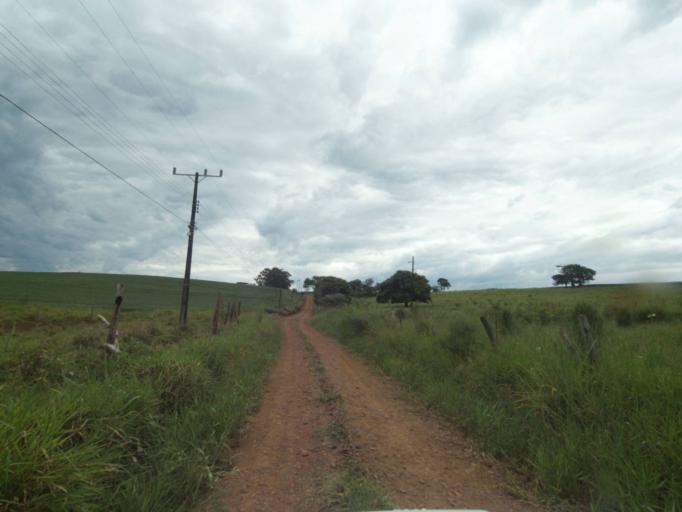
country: BR
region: Parana
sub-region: Guaraniacu
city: Guaraniacu
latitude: -24.9258
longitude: -52.9374
